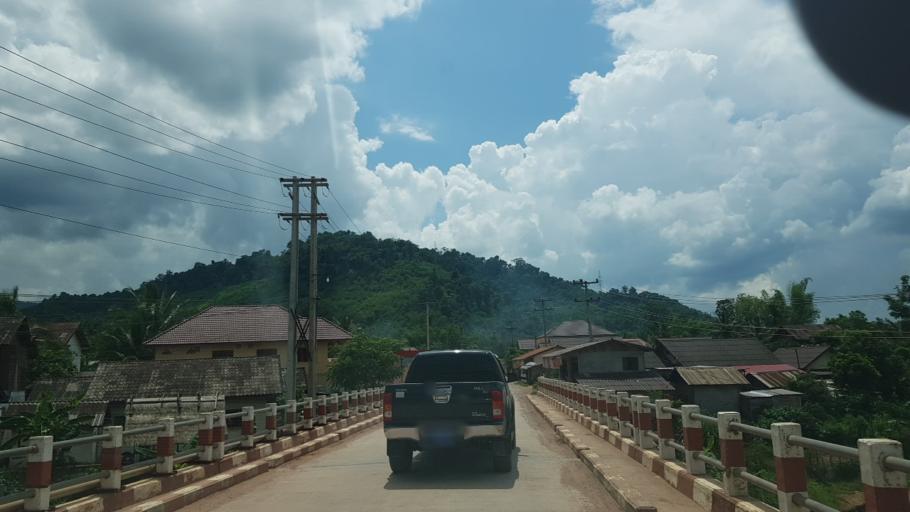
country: LA
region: Oudomxai
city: Muang Xay
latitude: 20.6628
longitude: 101.9748
